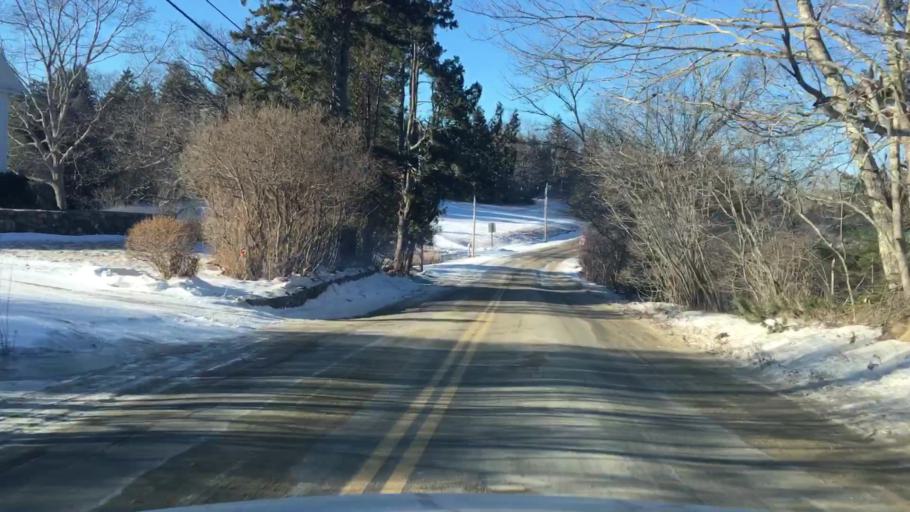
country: US
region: Maine
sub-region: Hancock County
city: Castine
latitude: 44.3469
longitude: -68.7467
